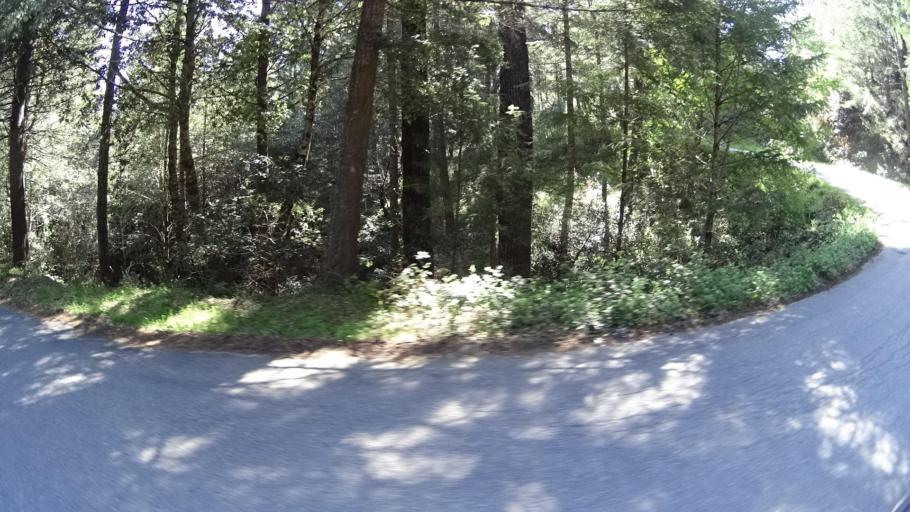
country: US
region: California
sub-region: Humboldt County
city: Redway
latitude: 40.0645
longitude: -123.6457
